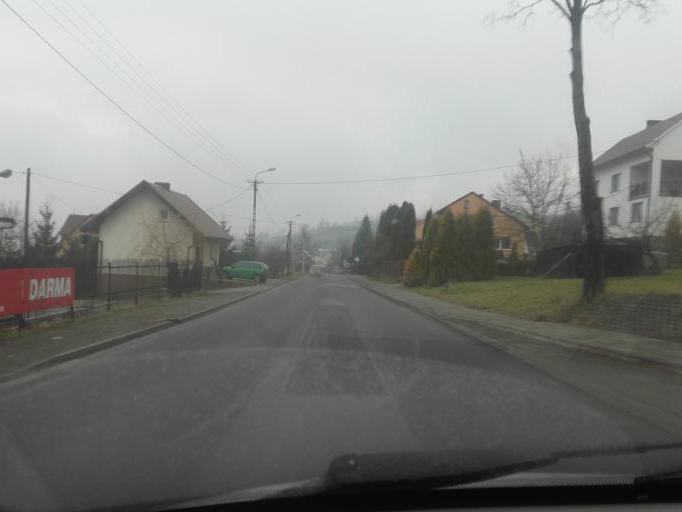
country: PL
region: Silesian Voivodeship
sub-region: Powiat cieszynski
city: Istebna
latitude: 49.5617
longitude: 18.9134
